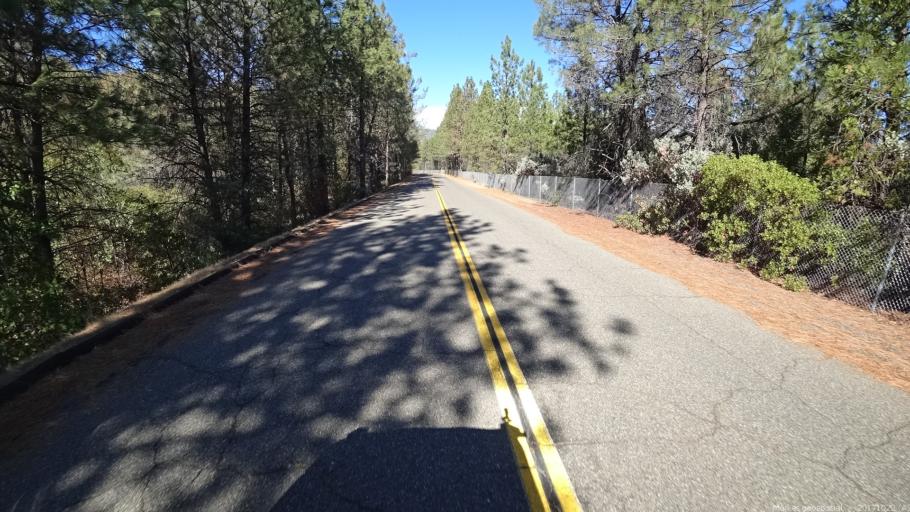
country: US
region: California
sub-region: Shasta County
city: Central Valley (historical)
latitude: 40.9072
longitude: -122.3850
